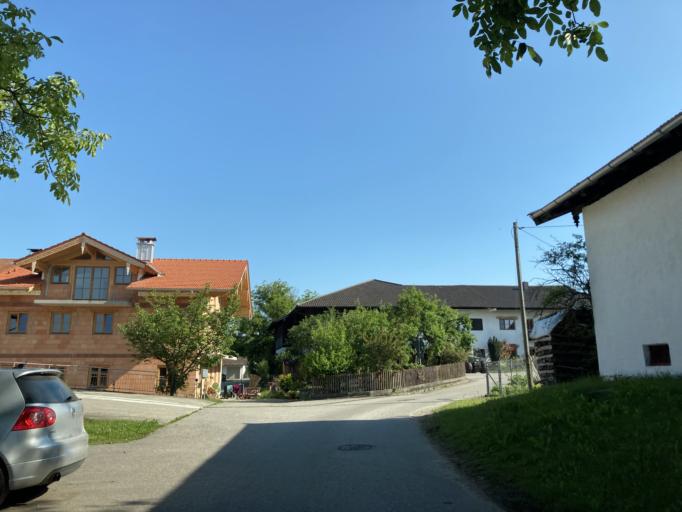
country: DE
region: Bavaria
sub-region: Upper Bavaria
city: Bad Endorf
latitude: 47.9106
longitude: 12.2818
